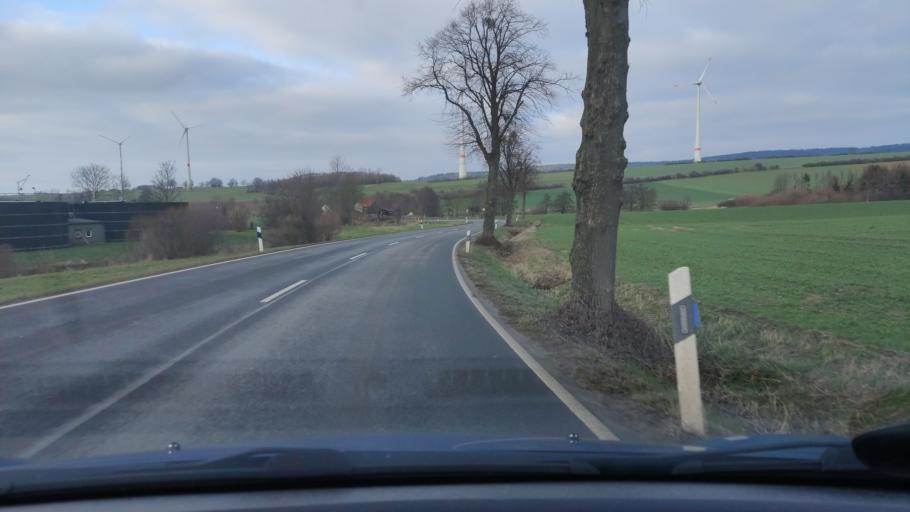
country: DE
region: Lower Saxony
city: Coppenbrugge
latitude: 52.1292
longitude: 9.5422
